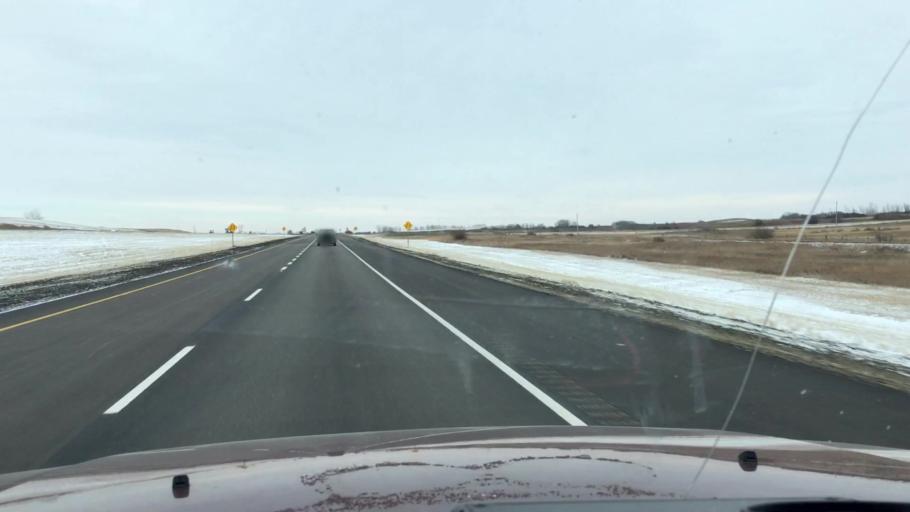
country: CA
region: Saskatchewan
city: Moose Jaw
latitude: 50.8656
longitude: -105.5971
